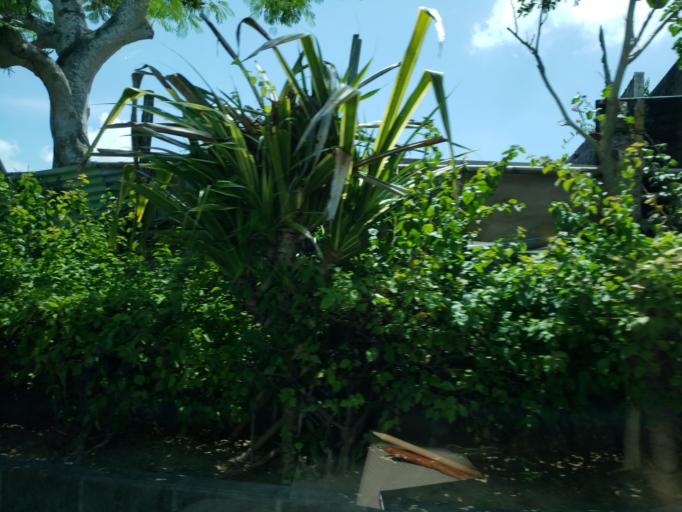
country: ID
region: Bali
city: Pecatu
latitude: -8.8425
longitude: 115.1218
